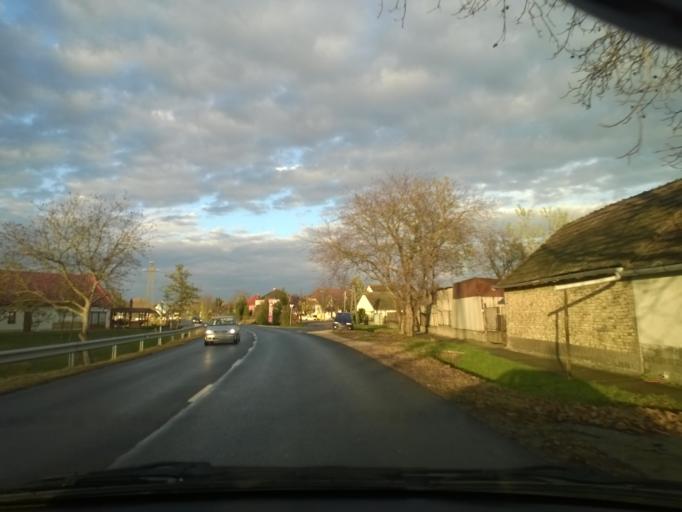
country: HU
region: Bacs-Kiskun
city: Dunapataj
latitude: 46.6492
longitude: 19.0022
